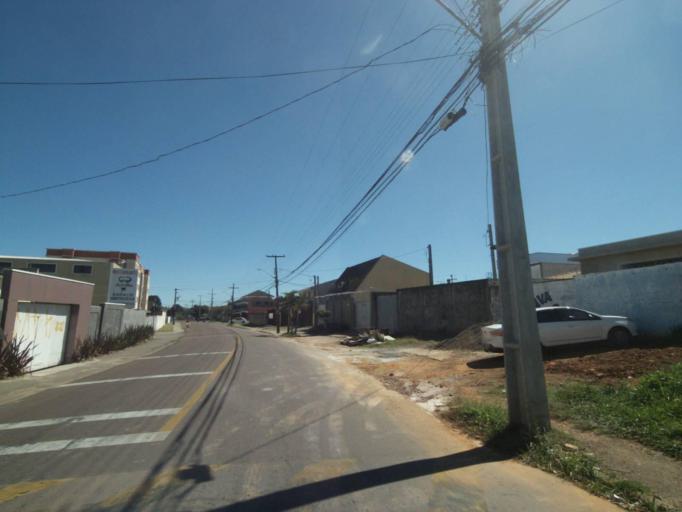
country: BR
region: Parana
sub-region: Curitiba
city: Curitiba
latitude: -25.4834
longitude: -49.3402
